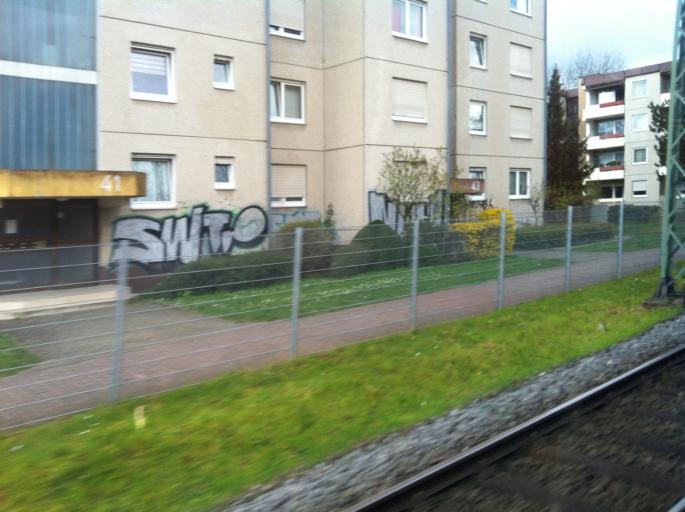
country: DE
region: Hesse
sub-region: Regierungsbezirk Darmstadt
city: Frankfurt am Main
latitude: 50.1636
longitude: 8.6451
